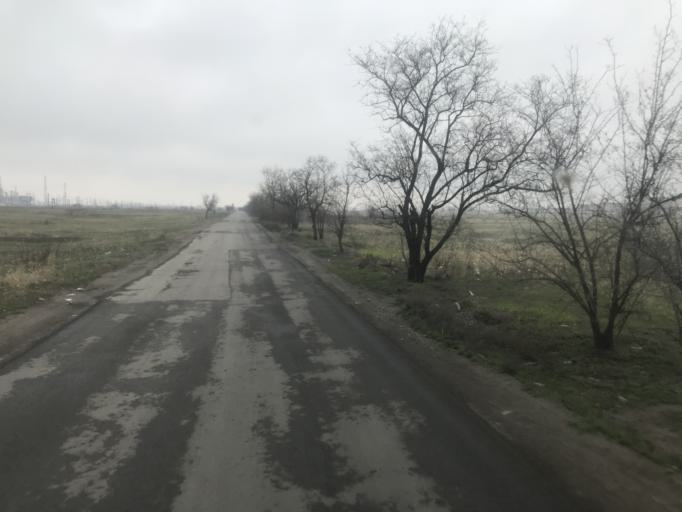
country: RU
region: Volgograd
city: Svetlyy Yar
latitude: 48.4961
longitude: 44.6516
